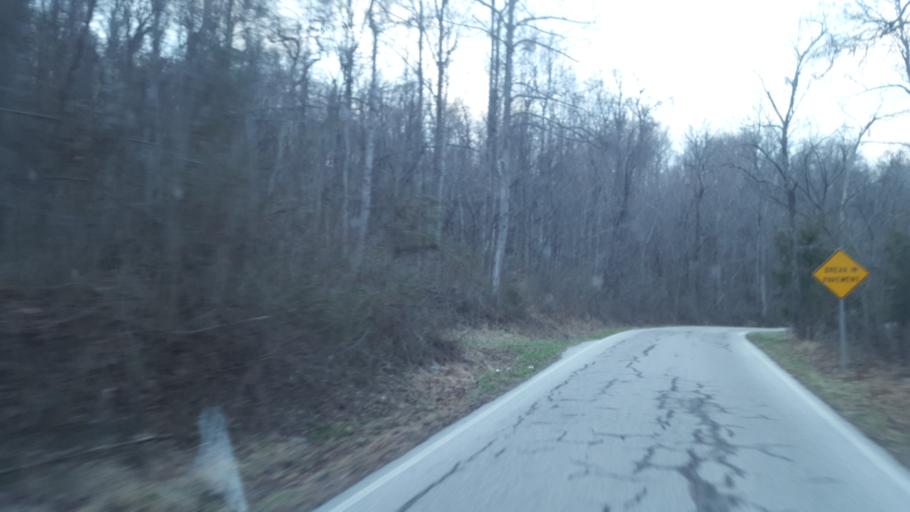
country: US
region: Ohio
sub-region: Adams County
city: Manchester
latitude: 38.5138
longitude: -83.5221
